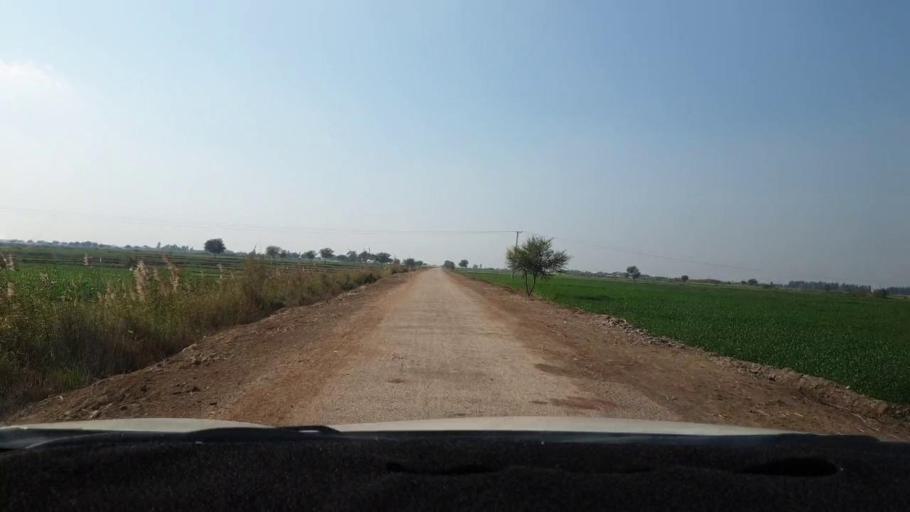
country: PK
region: Sindh
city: Berani
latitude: 25.7720
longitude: 68.8363
